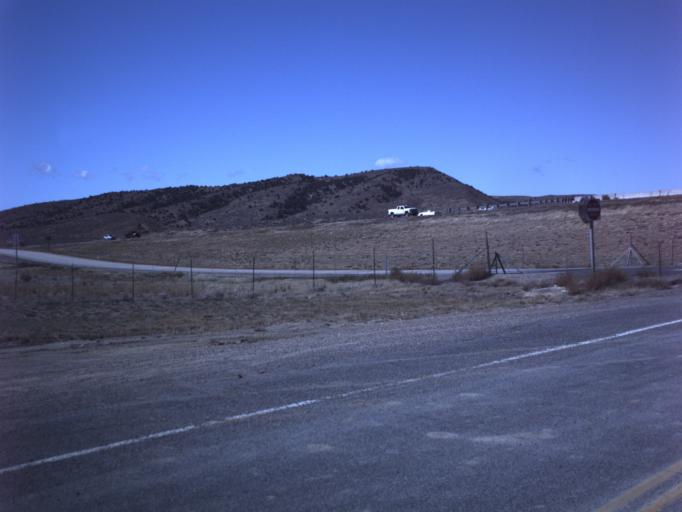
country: US
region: Utah
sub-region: Juab County
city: Nephi
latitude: 39.4826
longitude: -111.9776
